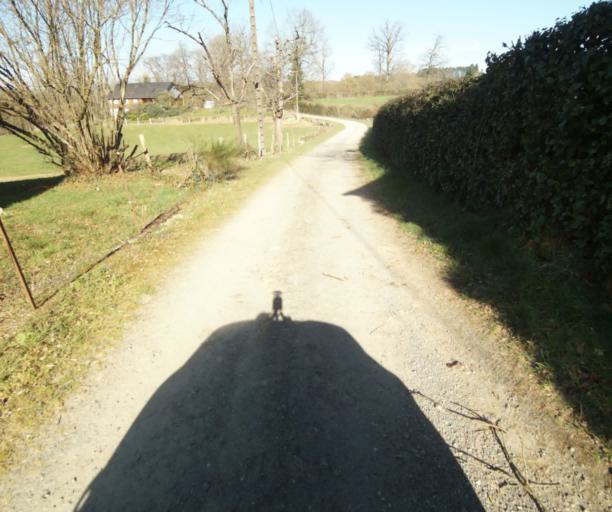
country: FR
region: Limousin
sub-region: Departement de la Correze
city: Chamboulive
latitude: 45.4739
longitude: 1.6873
